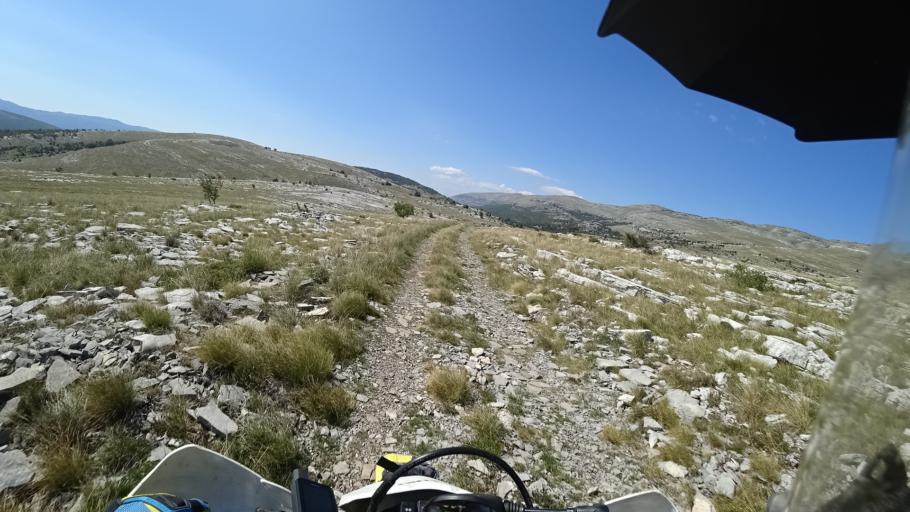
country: HR
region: Splitsko-Dalmatinska
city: Hrvace
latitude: 43.8999
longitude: 16.5975
